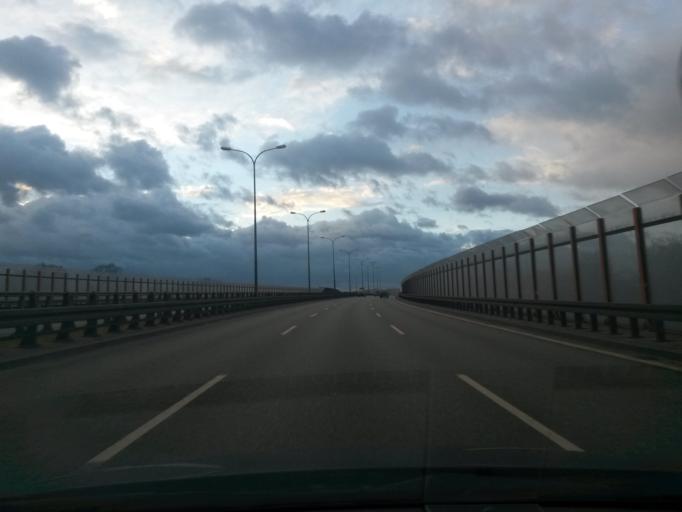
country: PL
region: Masovian Voivodeship
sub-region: Warszawa
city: Praga Poludnie
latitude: 52.2043
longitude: 21.0775
